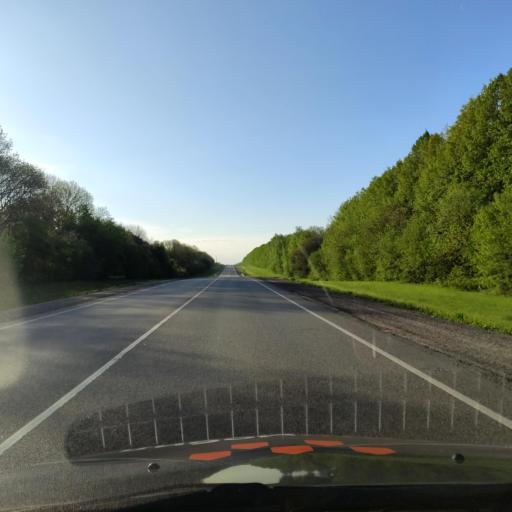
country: RU
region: Lipetsk
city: Yelets
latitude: 52.5711
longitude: 38.6598
